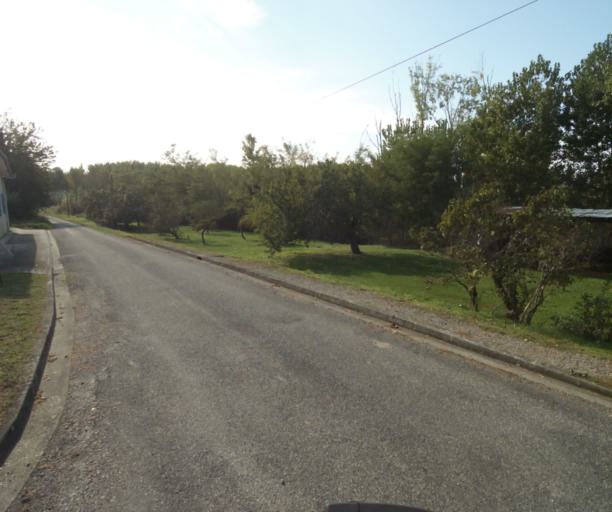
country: FR
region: Midi-Pyrenees
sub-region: Departement du Tarn-et-Garonne
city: Finhan
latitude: 43.9065
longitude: 1.2207
